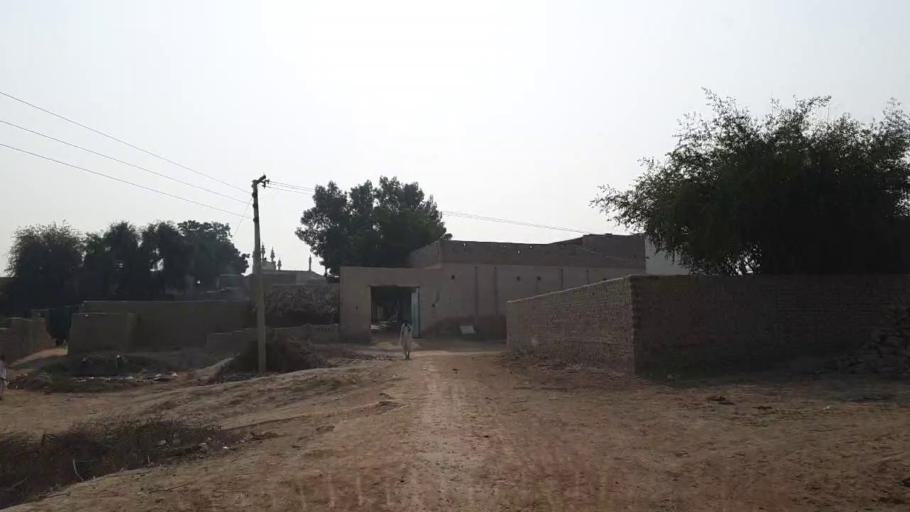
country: PK
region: Sindh
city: Bhan
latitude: 26.5171
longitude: 67.7349
